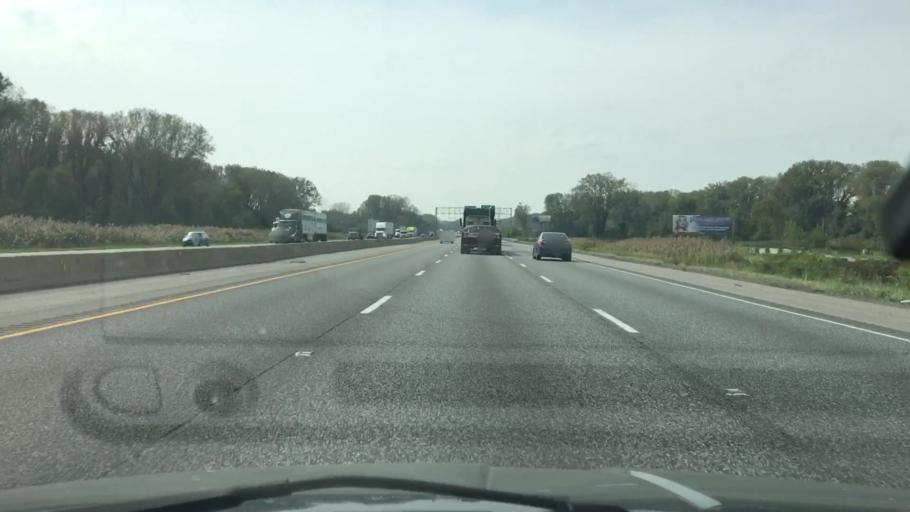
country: US
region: Indiana
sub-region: Porter County
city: Ogden Dunes
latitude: 41.5998
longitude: -87.1959
